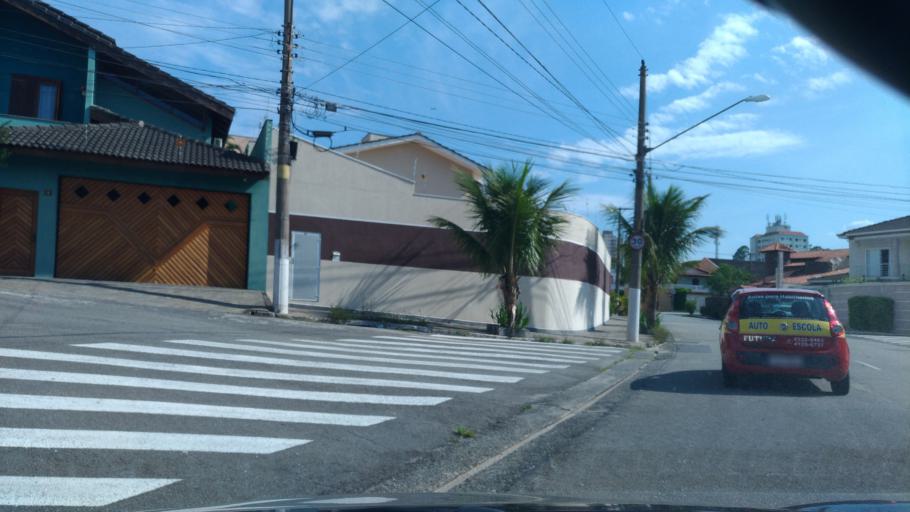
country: BR
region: Sao Paulo
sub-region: Sao Bernardo Do Campo
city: Sao Bernardo do Campo
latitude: -23.7102
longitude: -46.5773
